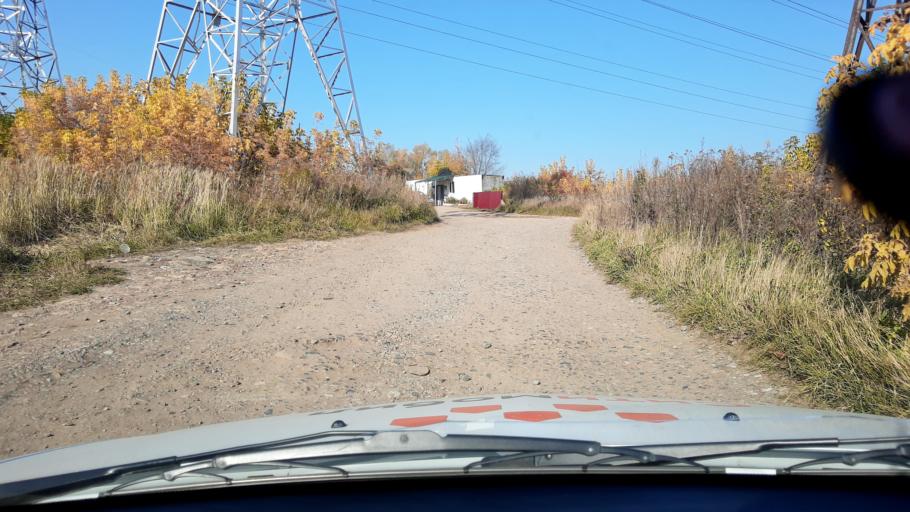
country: RU
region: Bashkortostan
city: Ufa
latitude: 54.8640
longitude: 56.1304
